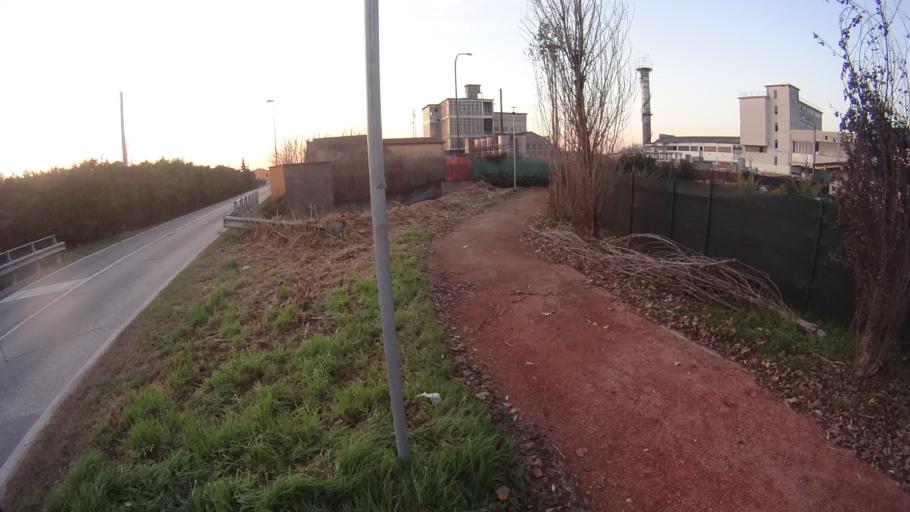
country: IT
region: Veneto
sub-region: Provincia di Verona
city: Povegliano Veronese
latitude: 45.3411
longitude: 10.8830
